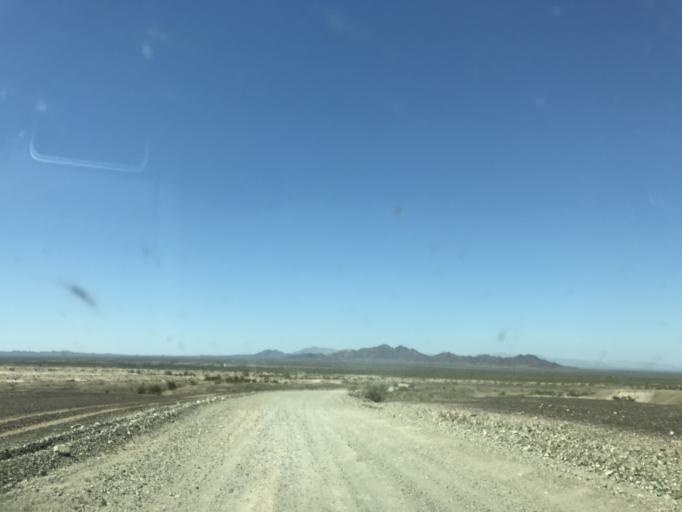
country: US
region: California
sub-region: Riverside County
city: Mesa Verde
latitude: 33.5007
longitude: -114.8548
